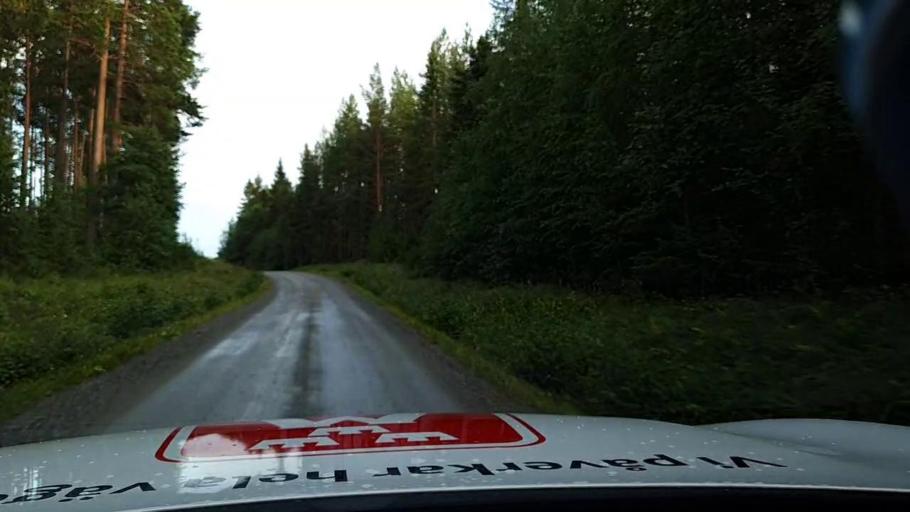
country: SE
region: Jaemtland
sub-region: Bergs Kommun
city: Hoverberg
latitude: 62.8672
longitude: 14.5257
